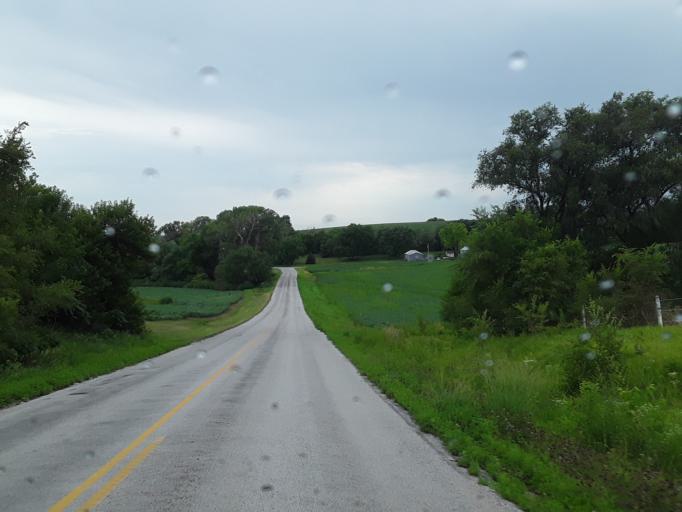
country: US
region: Nebraska
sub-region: Washington County
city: Blair
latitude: 41.5019
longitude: -96.1548
